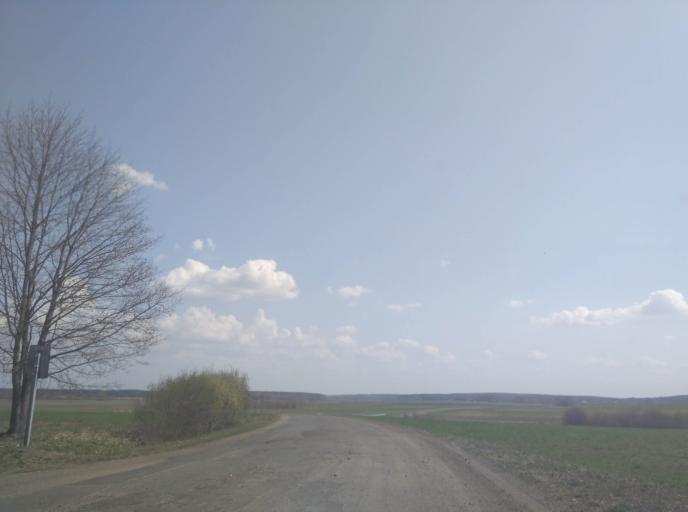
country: BY
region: Minsk
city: Loshnitsa
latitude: 54.4912
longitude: 28.7263
